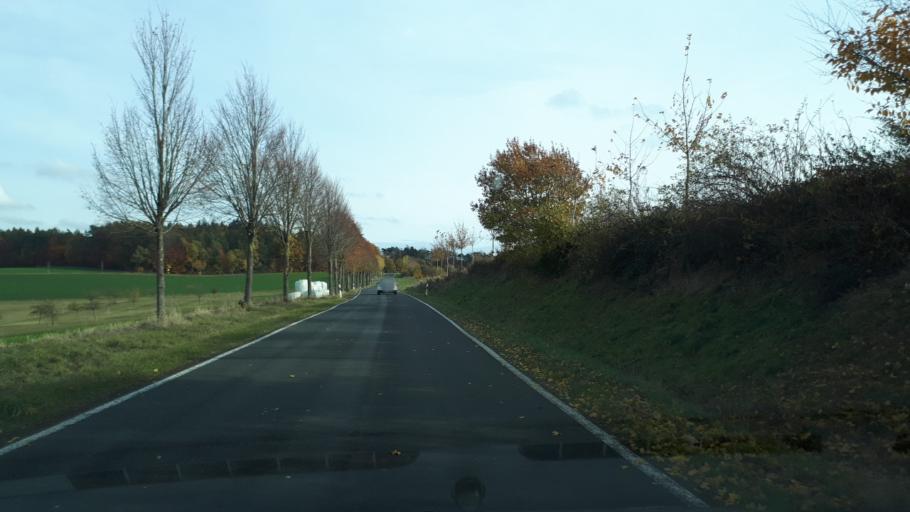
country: DE
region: Rheinland-Pfalz
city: Gillenbeuren
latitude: 50.1523
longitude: 7.0196
